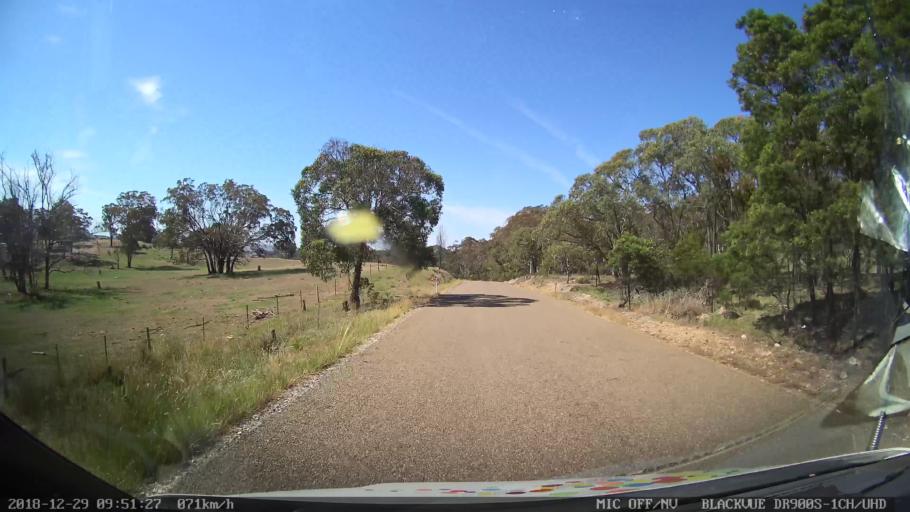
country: AU
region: New South Wales
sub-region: Goulburn Mulwaree
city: Goulburn
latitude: -34.7323
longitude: 149.4616
